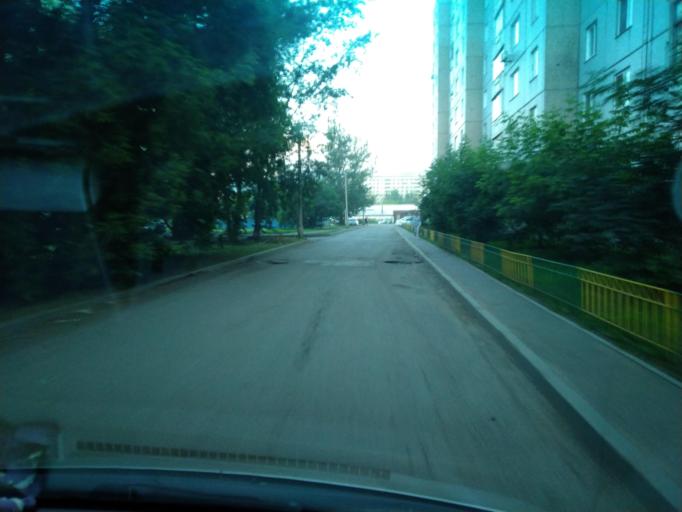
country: RU
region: Krasnoyarskiy
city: Krasnoyarsk
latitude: 55.9870
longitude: 92.8701
